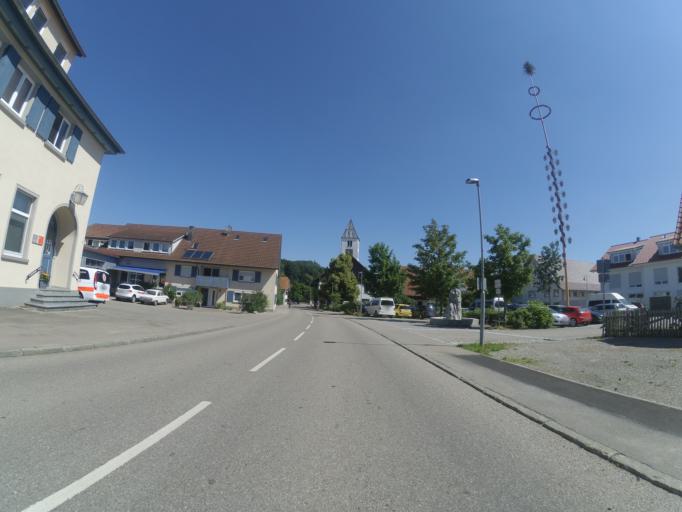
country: DE
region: Baden-Wuerttemberg
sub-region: Tuebingen Region
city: Leutkirch im Allgau
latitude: 47.8454
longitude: 9.9704
